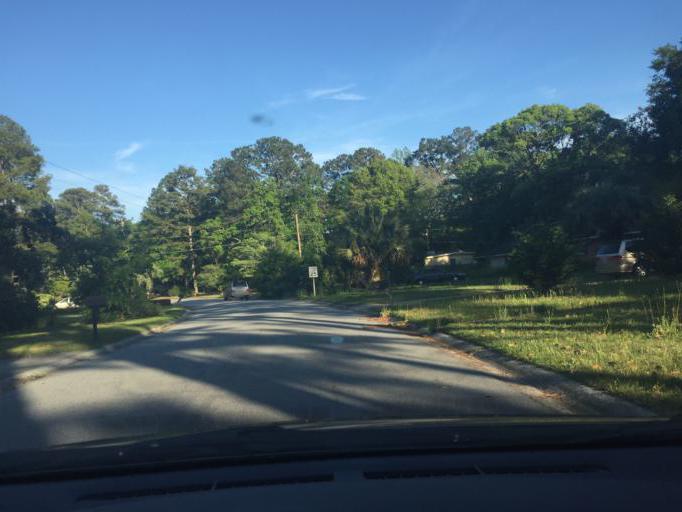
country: US
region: Georgia
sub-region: Chatham County
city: Montgomery
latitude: 31.9815
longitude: -81.1112
